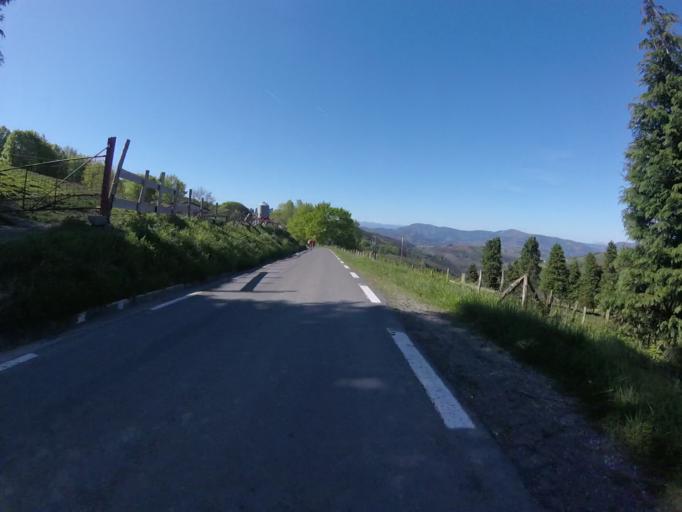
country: ES
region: Basque Country
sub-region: Provincia de Guipuzcoa
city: Errezil
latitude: 43.1998
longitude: -2.2014
